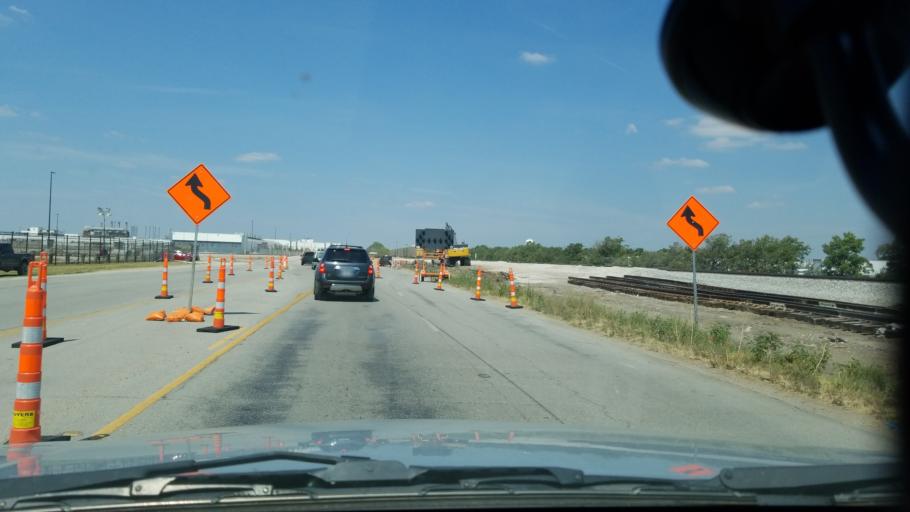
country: US
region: Texas
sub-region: Dallas County
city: Grand Prairie
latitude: 32.7459
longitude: -96.9715
